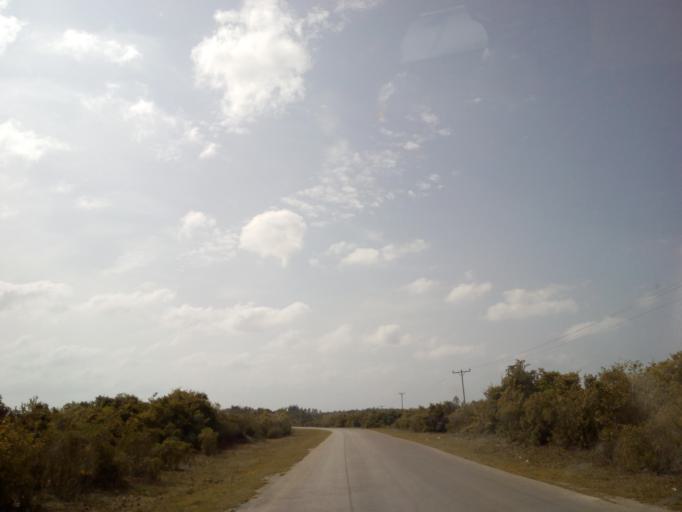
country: TZ
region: Zanzibar Central/South
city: Koani
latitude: -6.2800
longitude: 39.3661
